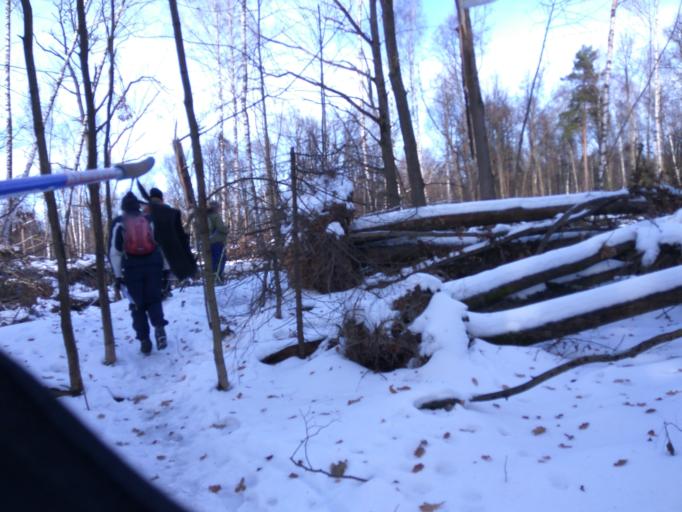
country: RU
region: Moskovskaya
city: Bogorodskoye
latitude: 55.8376
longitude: 37.7105
